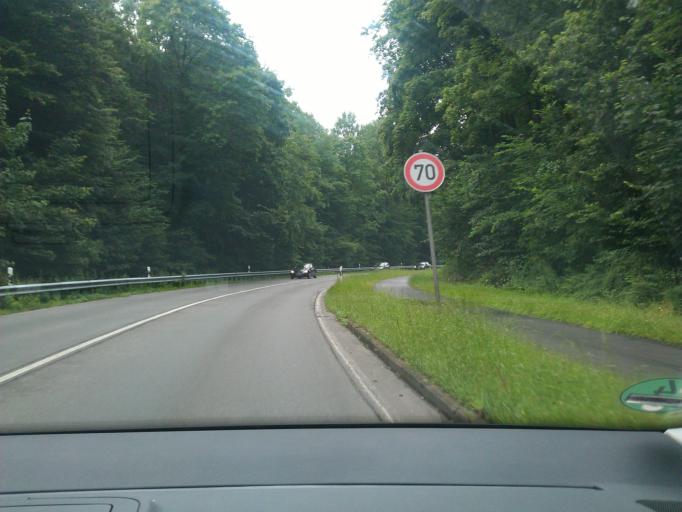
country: DE
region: North Rhine-Westphalia
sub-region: Regierungsbezirk Koln
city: Aachen
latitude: 50.7444
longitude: 6.1082
